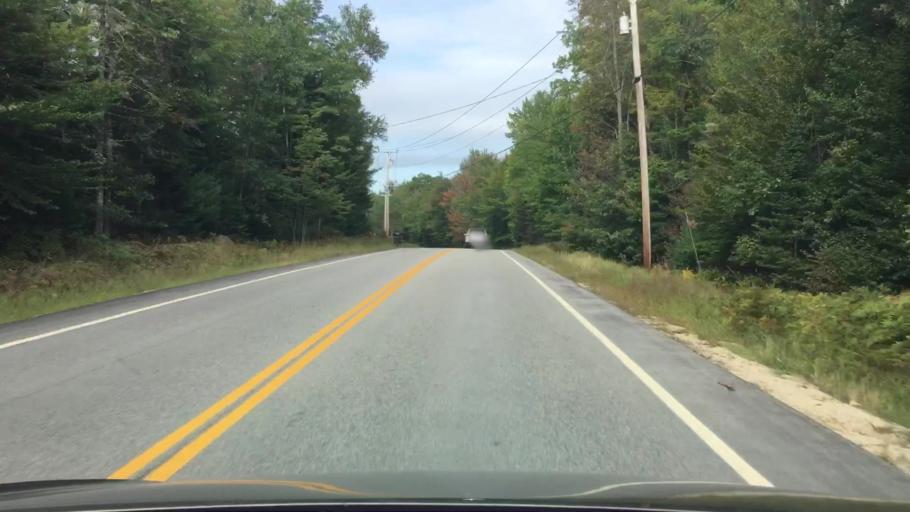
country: US
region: Maine
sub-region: Oxford County
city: Hartford
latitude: 44.3672
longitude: -70.3391
